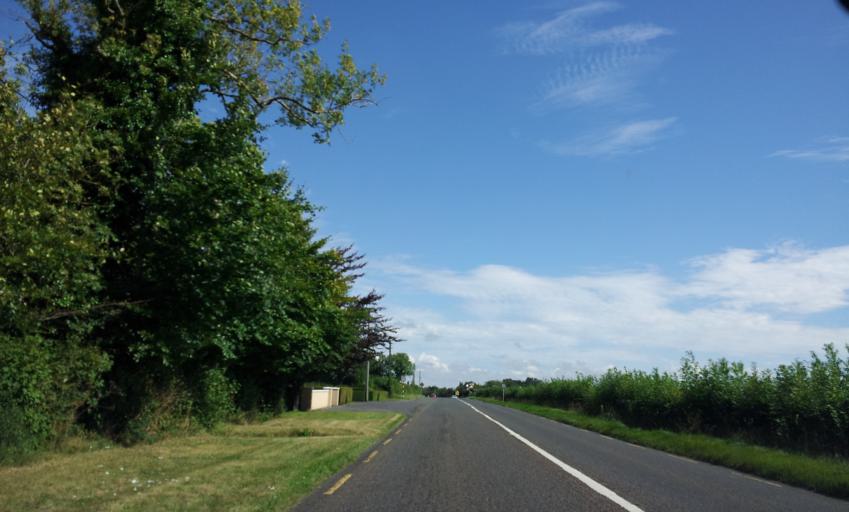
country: IE
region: Leinster
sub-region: Laois
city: Portlaoise
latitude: 53.0288
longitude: -7.3338
